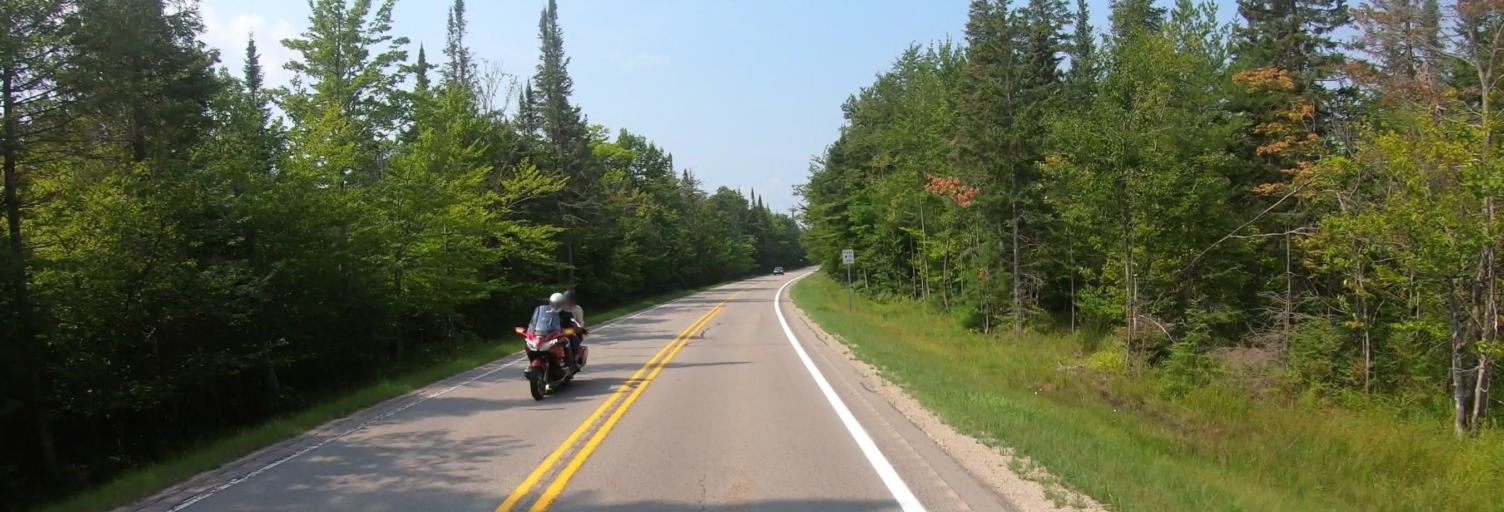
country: US
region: Michigan
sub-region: Luce County
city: Newberry
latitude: 46.5796
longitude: -85.2590
